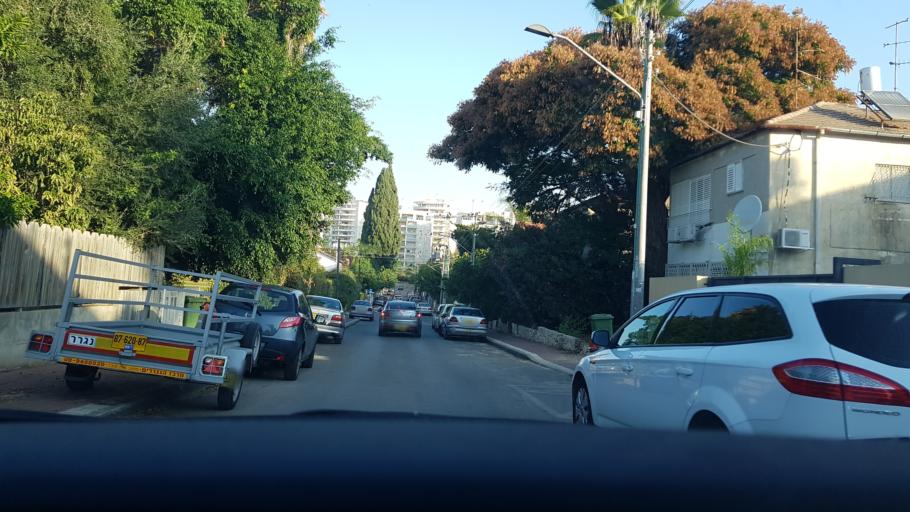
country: IL
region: Central District
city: Ness Ziona
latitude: 31.8959
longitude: 34.8227
